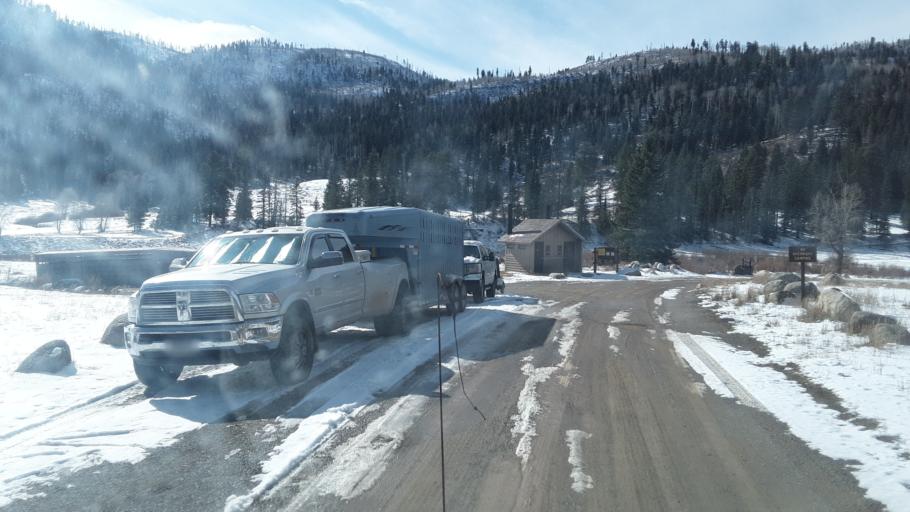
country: US
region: Colorado
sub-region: La Plata County
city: Bayfield
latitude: 37.4233
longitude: -107.6703
